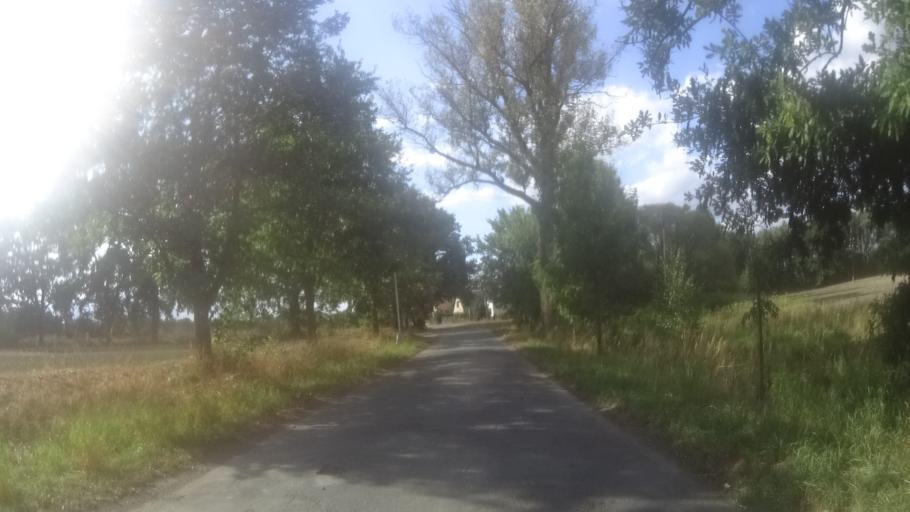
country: CZ
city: Albrechtice nad Orlici
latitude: 50.1548
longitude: 16.0477
